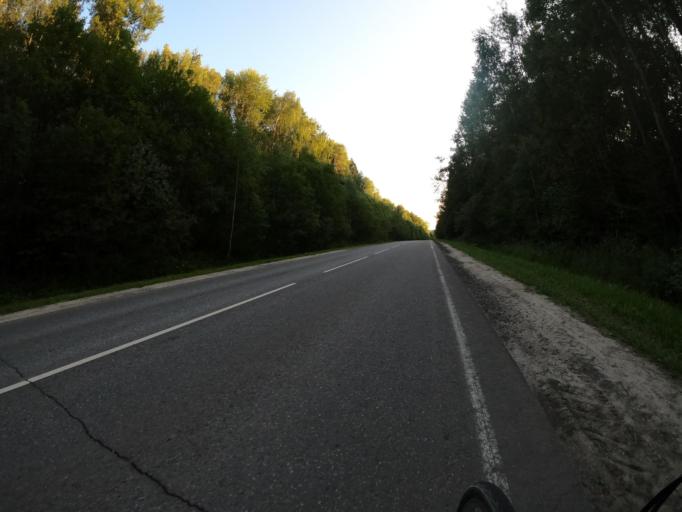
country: RU
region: Moskovskaya
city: Meshcherino
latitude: 55.1092
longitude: 38.3061
